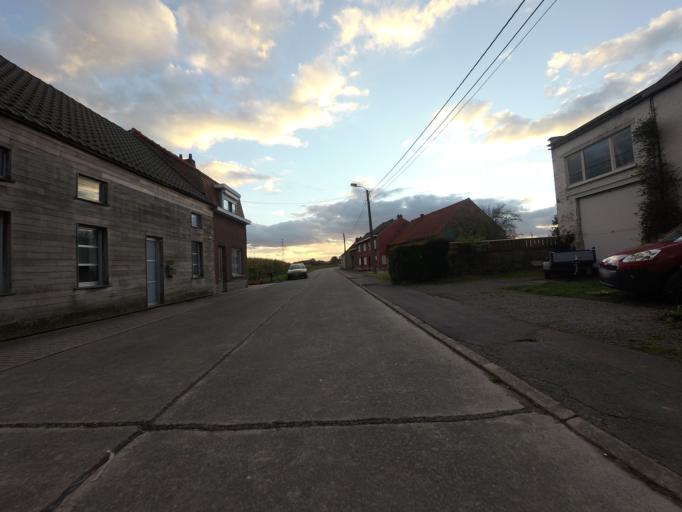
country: BE
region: Flanders
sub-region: Provincie Vlaams-Brabant
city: Kapelle-op-den-Bos
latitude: 51.0312
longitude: 4.3906
